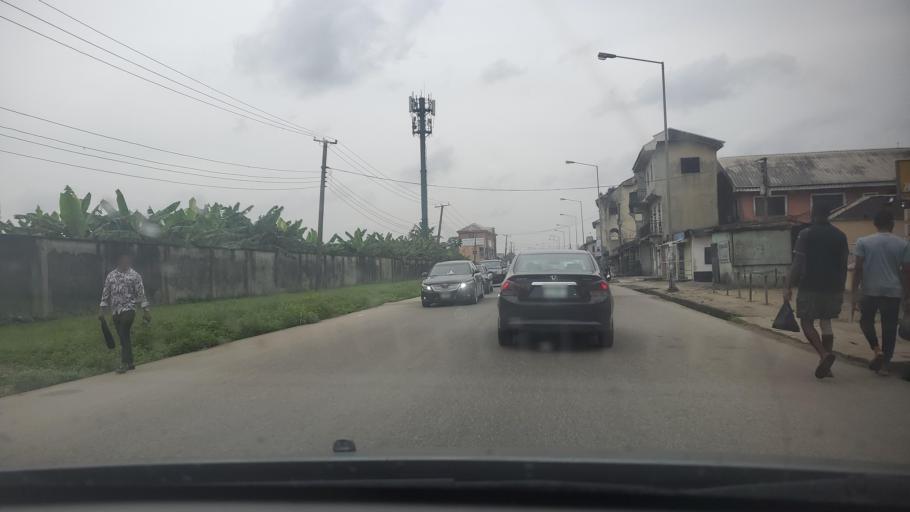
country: NG
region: Rivers
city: Port Harcourt
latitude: 4.8443
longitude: 6.9938
